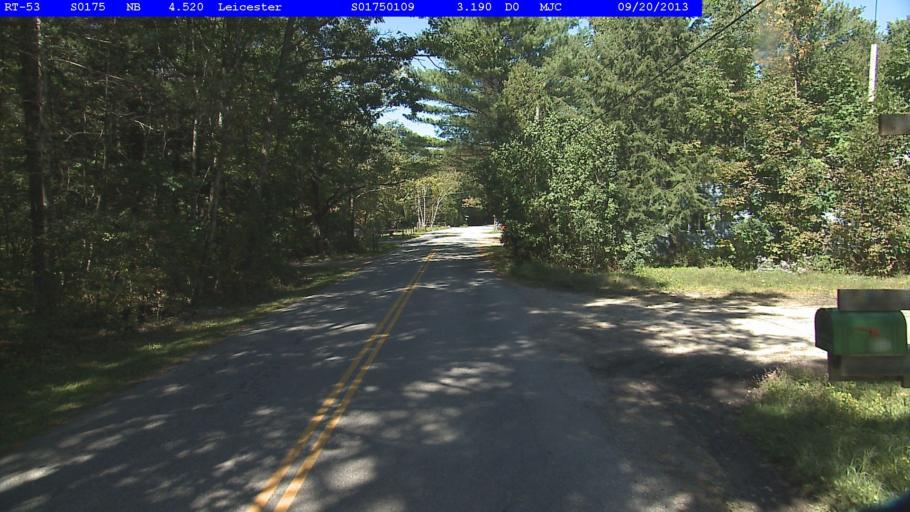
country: US
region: Vermont
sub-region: Rutland County
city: Brandon
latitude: 43.8885
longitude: -73.0645
